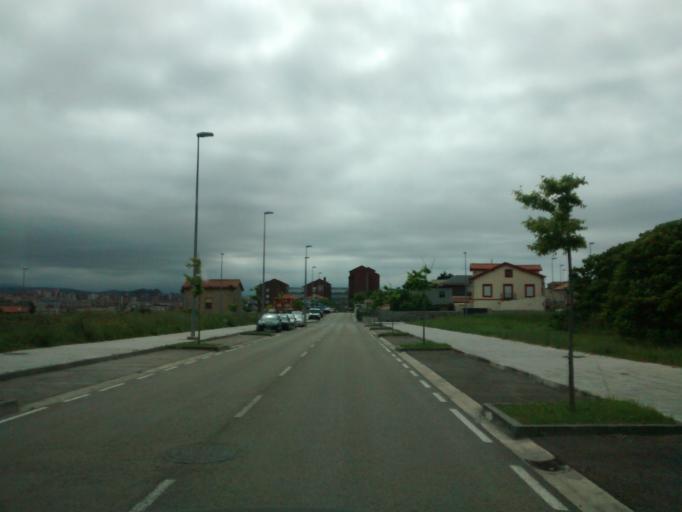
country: ES
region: Cantabria
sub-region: Provincia de Cantabria
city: Santander
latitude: 43.4790
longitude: -3.8071
